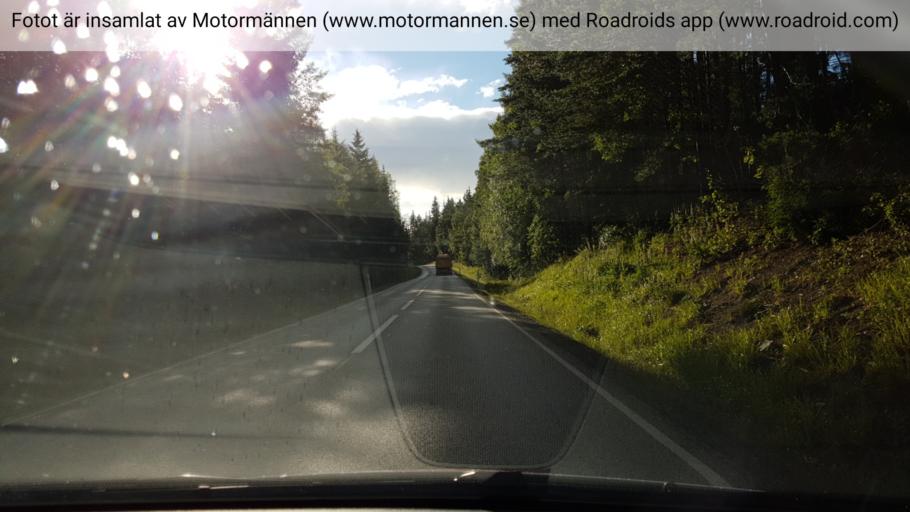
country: SE
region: OErebro
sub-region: Hallefors Kommun
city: Haellefors
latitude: 59.8007
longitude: 14.7280
